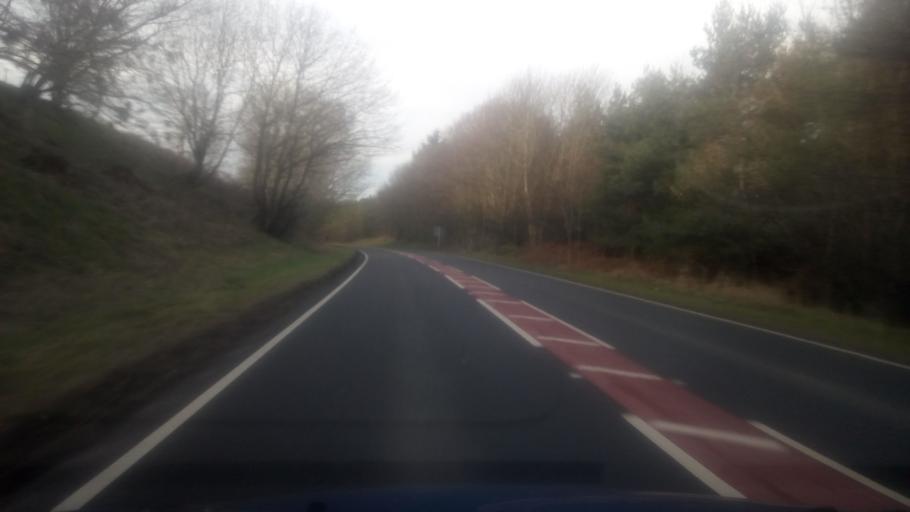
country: GB
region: Scotland
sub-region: The Scottish Borders
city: Jedburgh
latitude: 55.4383
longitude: -2.5437
